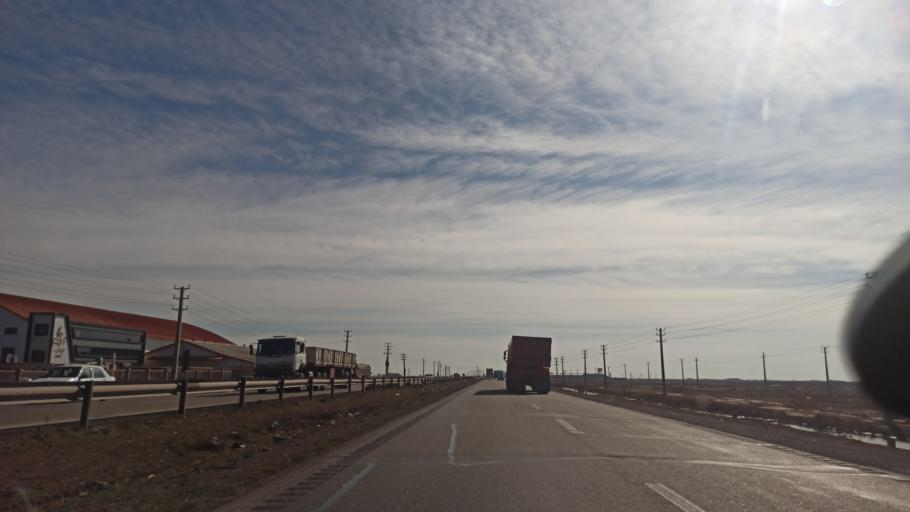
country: IR
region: Qazvin
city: Alvand
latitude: 36.1012
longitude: 50.0445
